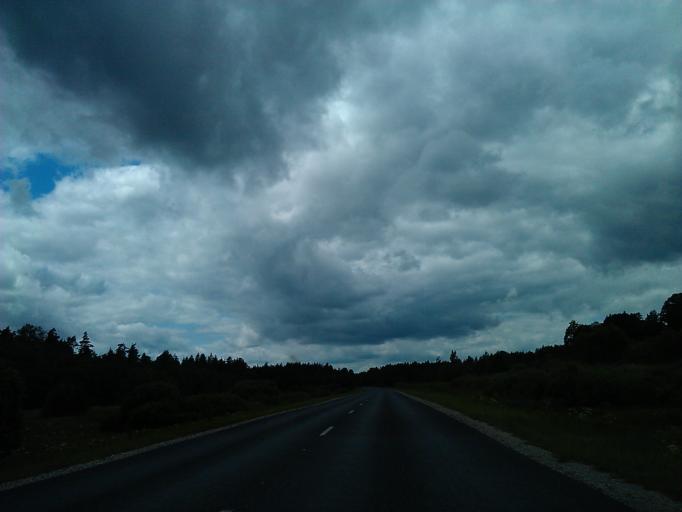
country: LV
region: Talsu Rajons
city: Stende
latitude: 57.0906
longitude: 22.3536
